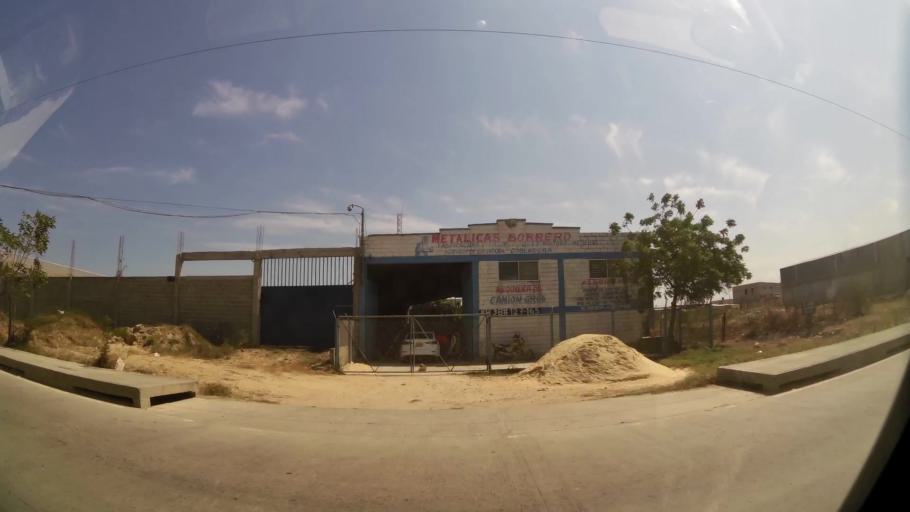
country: CO
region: Atlantico
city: Barranquilla
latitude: 10.9790
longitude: -74.8487
